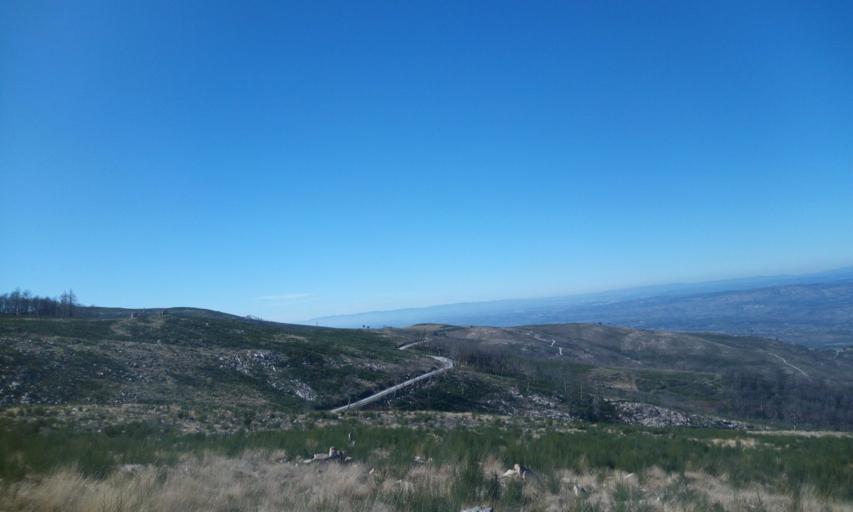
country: PT
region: Guarda
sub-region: Manteigas
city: Manteigas
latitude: 40.4946
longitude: -7.5234
